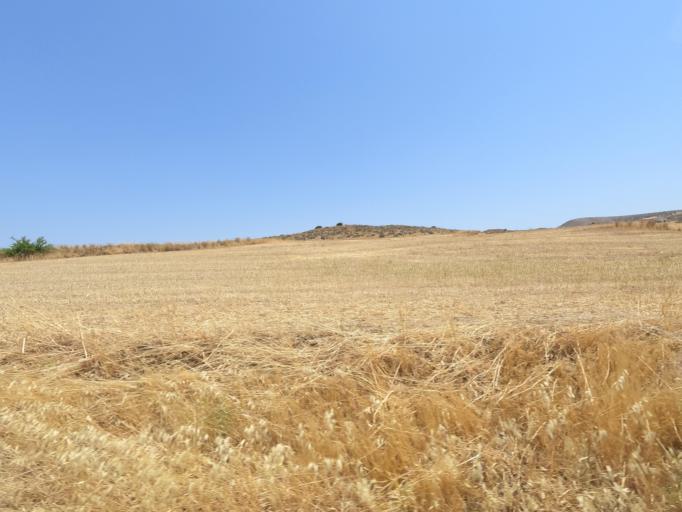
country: CY
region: Larnaka
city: Troulloi
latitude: 35.0201
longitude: 33.6381
